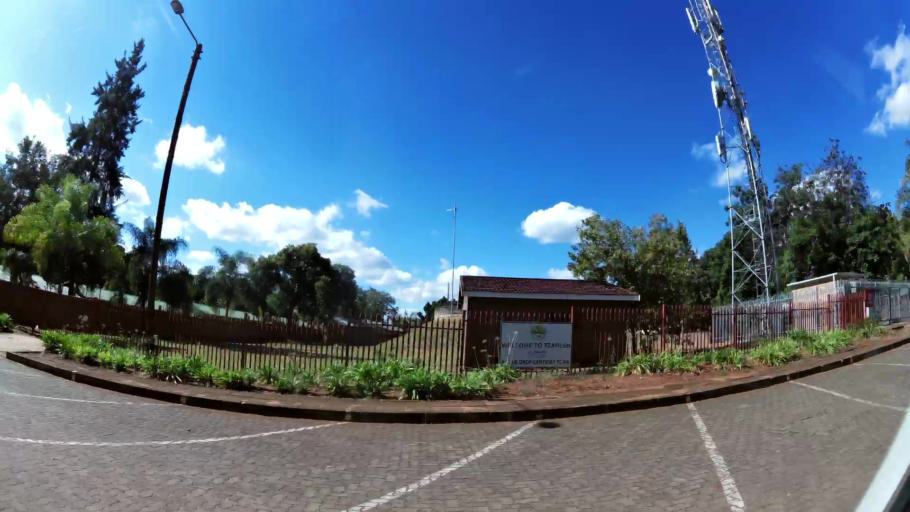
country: ZA
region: Limpopo
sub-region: Mopani District Municipality
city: Tzaneen
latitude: -23.8363
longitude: 30.1532
